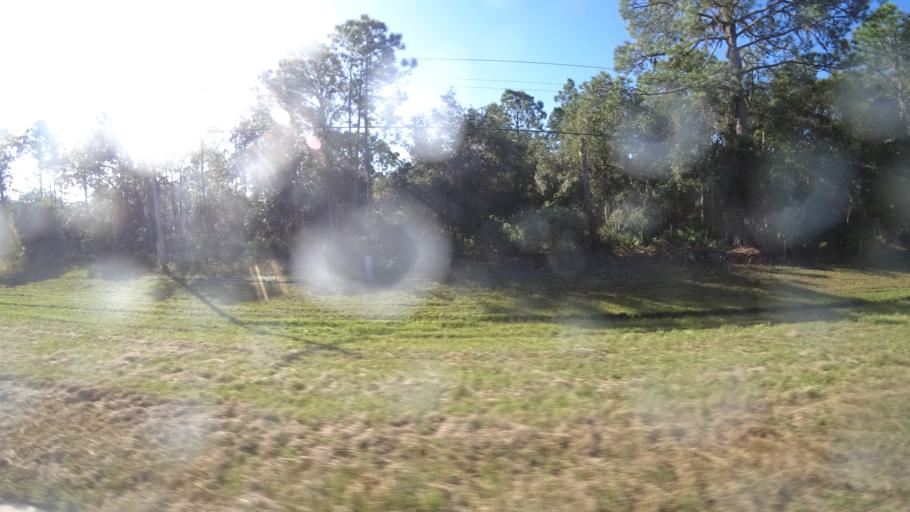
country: US
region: Florida
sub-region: Hillsborough County
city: Sun City Center
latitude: 27.6575
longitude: -82.3759
